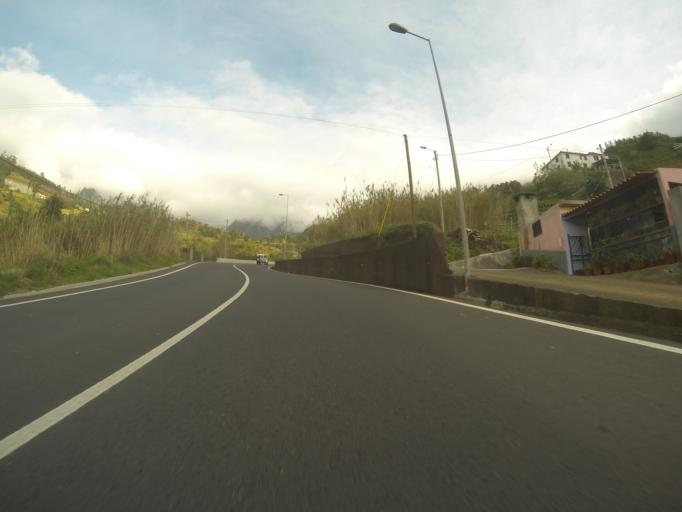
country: PT
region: Madeira
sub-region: Sao Vicente
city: Sao Vicente
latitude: 32.7749
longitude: -17.0321
